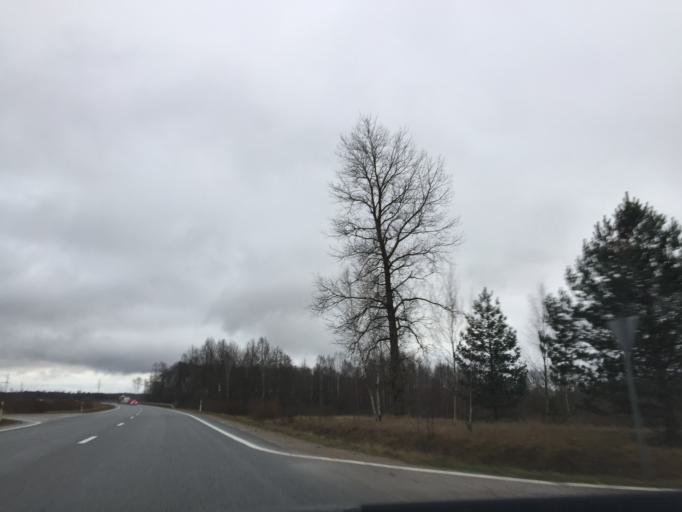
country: LV
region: Broceni
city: Broceni
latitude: 56.6703
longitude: 22.5894
